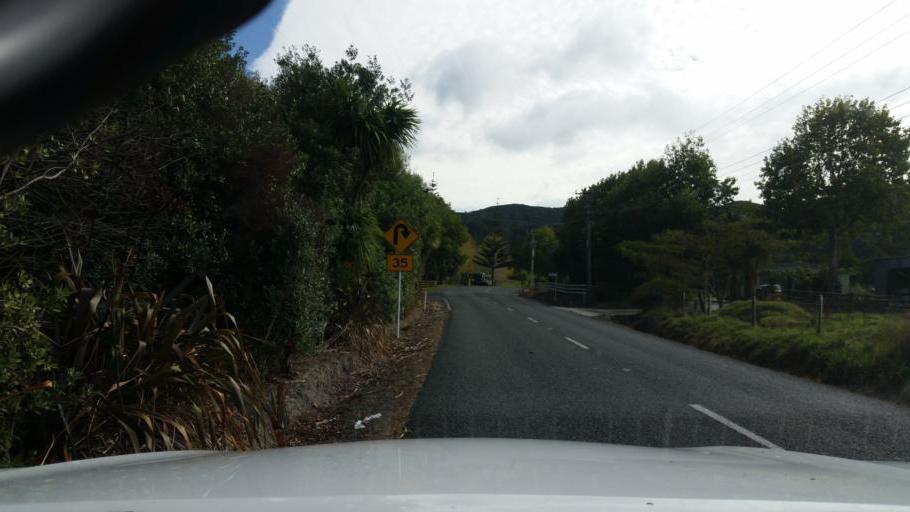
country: NZ
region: Northland
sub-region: Whangarei
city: Ruakaka
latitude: -36.0853
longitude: 174.5354
